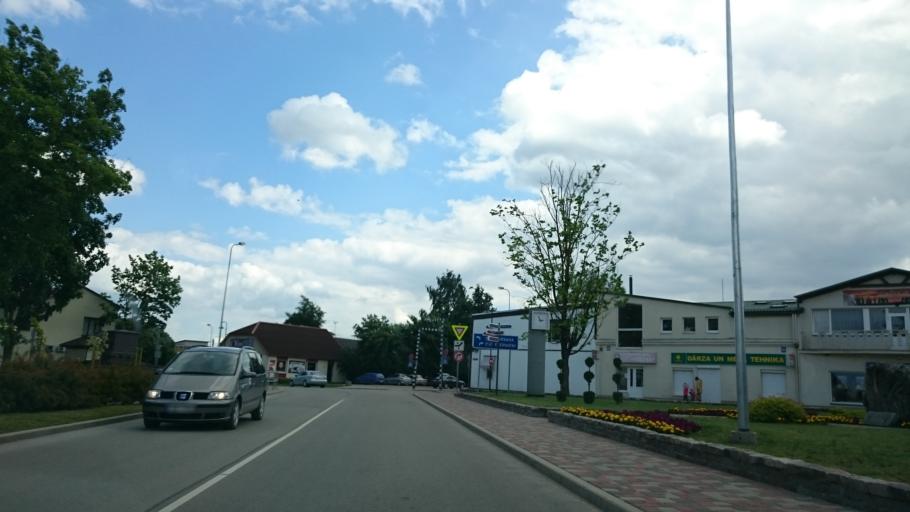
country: LV
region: Ludzas Rajons
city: Ludza
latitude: 56.5470
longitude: 27.7250
